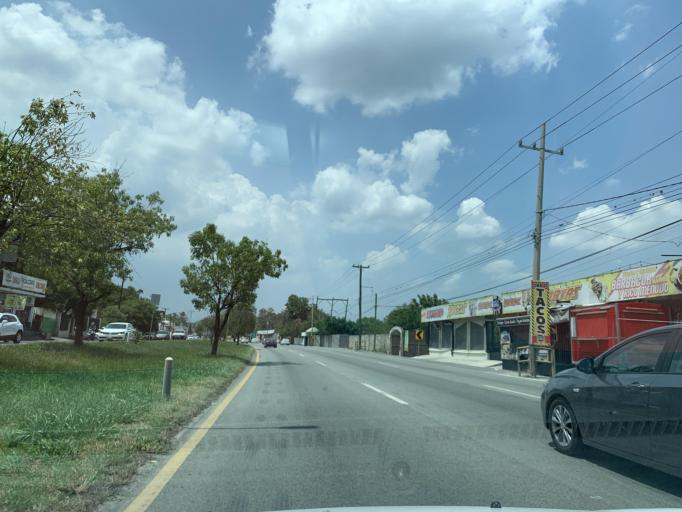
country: MX
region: Nuevo Leon
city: Santiago
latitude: 25.4185
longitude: -100.1429
